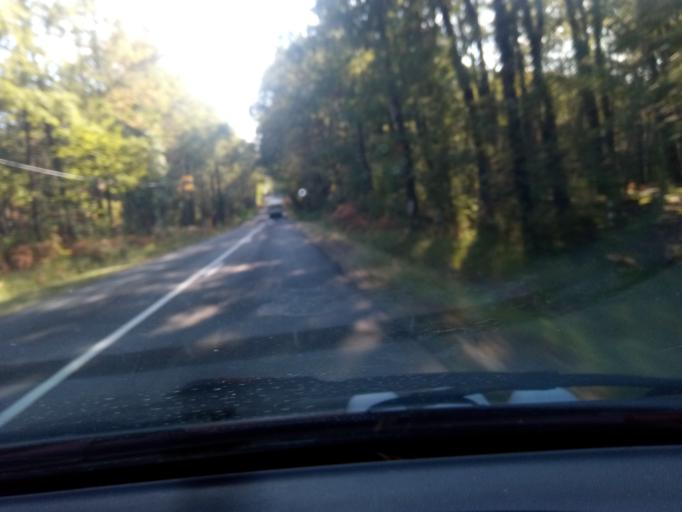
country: FR
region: Poitou-Charentes
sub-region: Departement de la Vienne
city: Lussac-les-Chateaux
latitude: 46.4239
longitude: 0.7171
